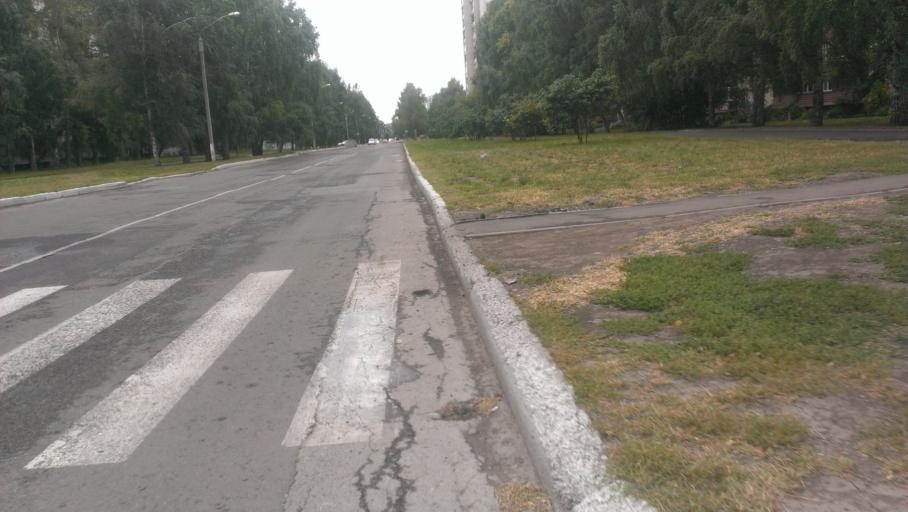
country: RU
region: Altai Krai
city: Novosilikatnyy
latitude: 53.3712
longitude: 83.6695
